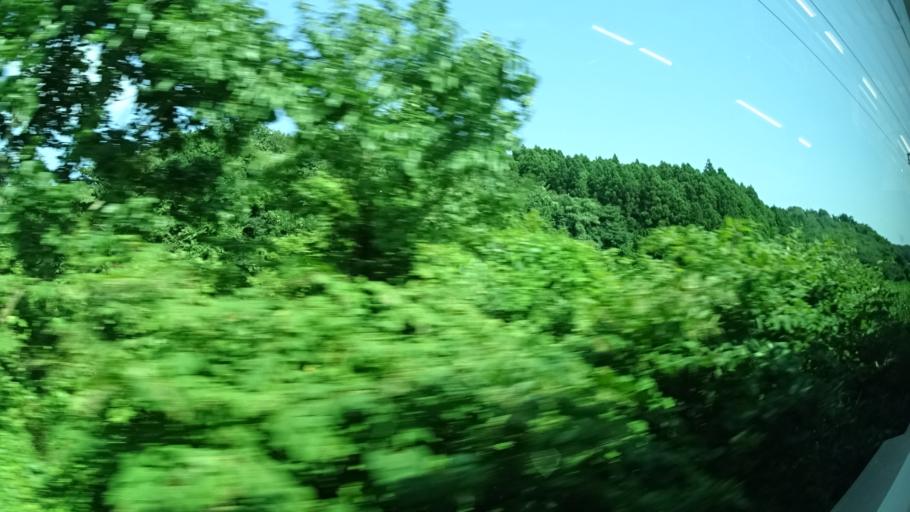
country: JP
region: Miyagi
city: Kogota
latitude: 38.4944
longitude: 141.0880
